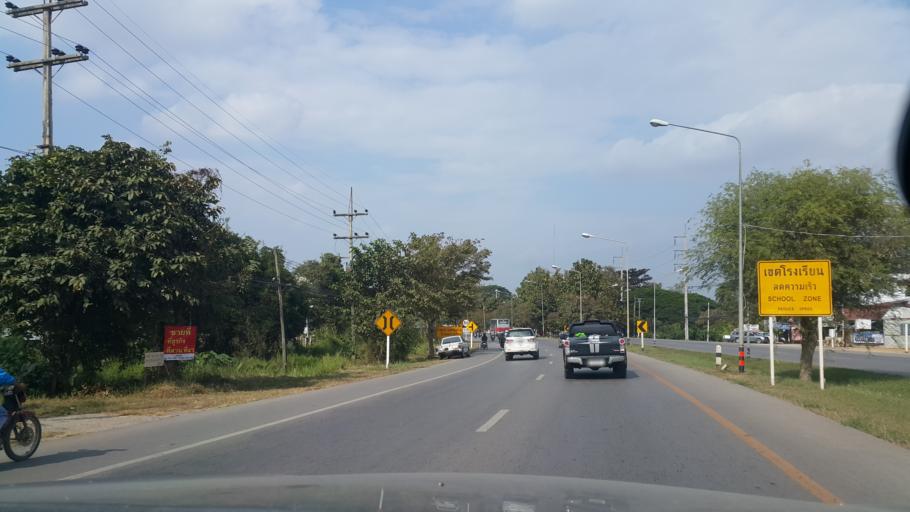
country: TH
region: Phayao
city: Phayao
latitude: 19.1573
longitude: 99.9140
